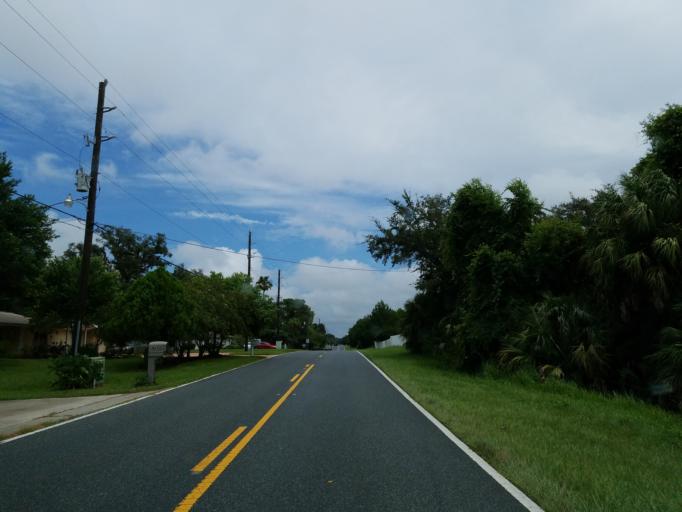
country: US
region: Florida
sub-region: Citrus County
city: Inverness
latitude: 28.8105
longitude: -82.2915
